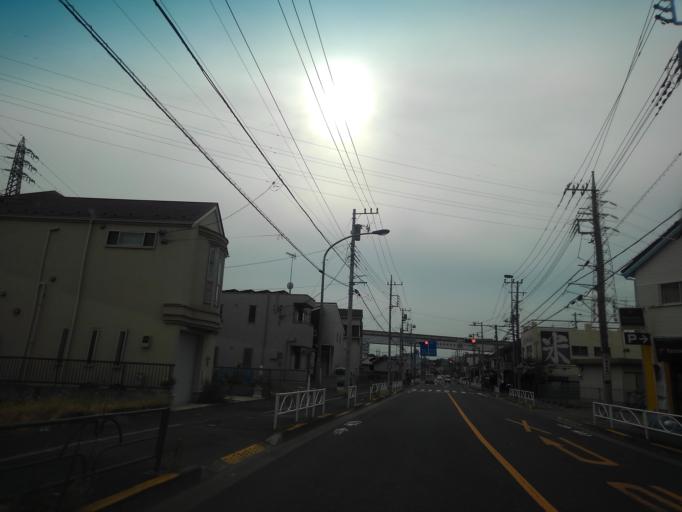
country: JP
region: Tokyo
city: Hino
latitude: 35.6796
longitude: 139.4097
